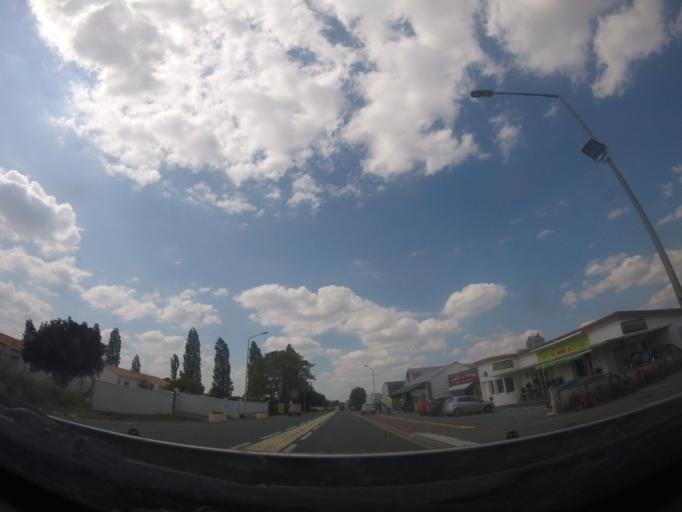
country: FR
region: Poitou-Charentes
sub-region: Departement de la Charente-Maritime
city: Bords
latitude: 45.8567
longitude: -0.8309
